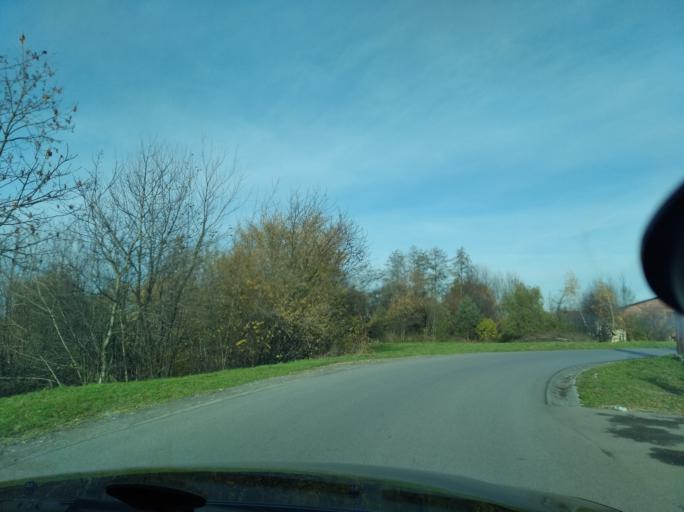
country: PL
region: Subcarpathian Voivodeship
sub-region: Powiat rzeszowski
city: Krasne
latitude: 50.0268
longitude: 22.1055
